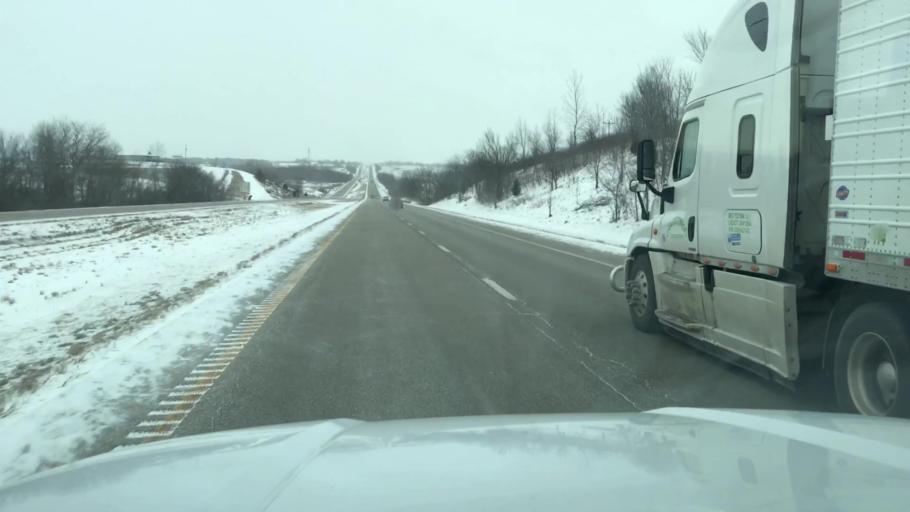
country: US
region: Missouri
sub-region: Clinton County
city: Gower
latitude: 39.7475
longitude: -94.6789
